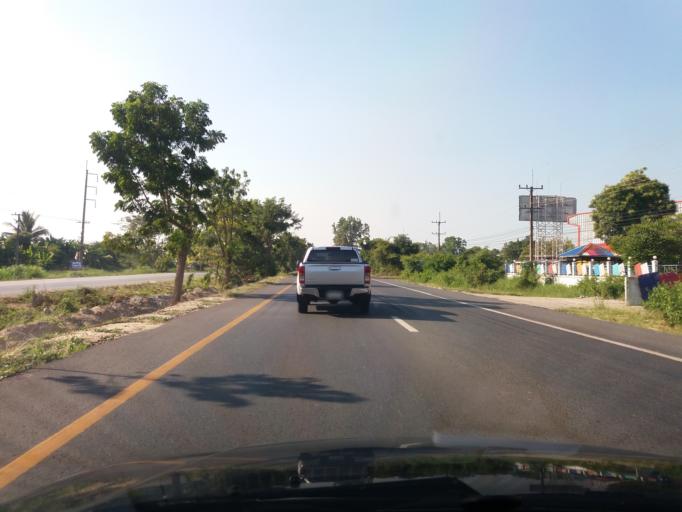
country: TH
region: Nakhon Sawan
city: Kao Liao
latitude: 15.7522
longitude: 100.0026
